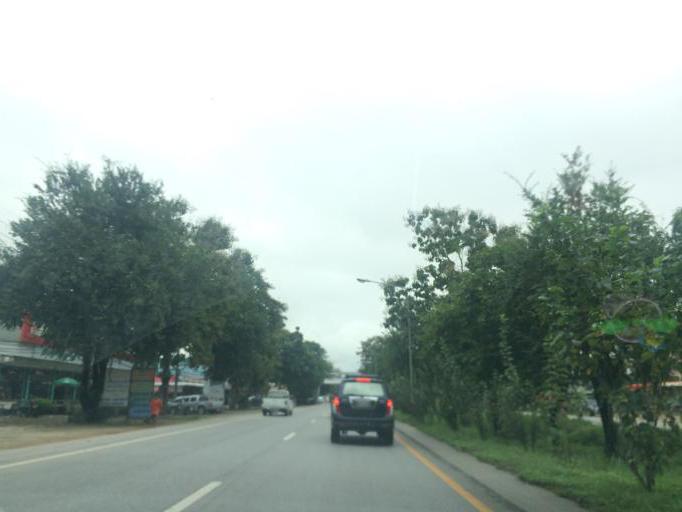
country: TH
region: Chiang Rai
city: Mae Lao
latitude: 19.7729
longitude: 99.7385
